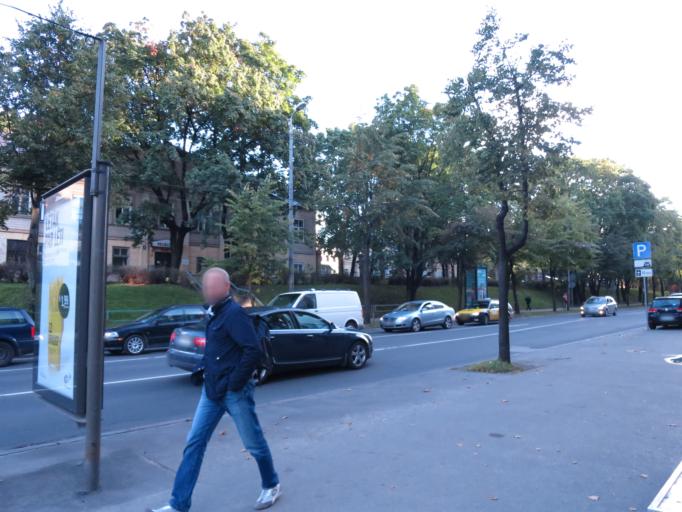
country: LV
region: Riga
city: Riga
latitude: 56.9627
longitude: 24.1242
